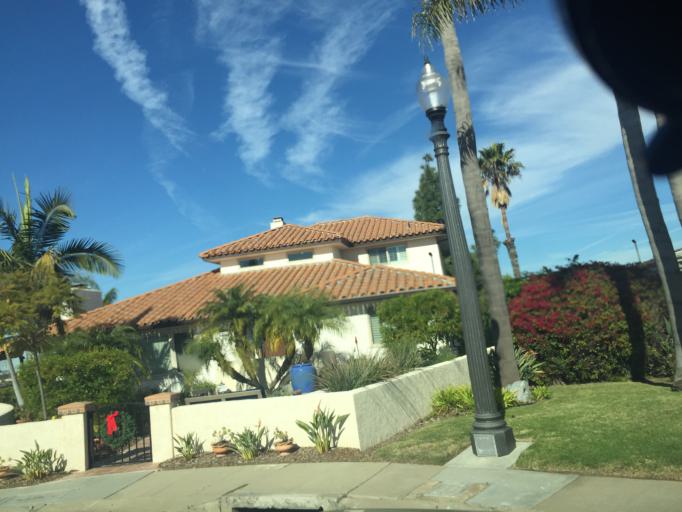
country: US
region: California
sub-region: San Diego County
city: Lemon Grove
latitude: 32.7674
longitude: -117.0872
